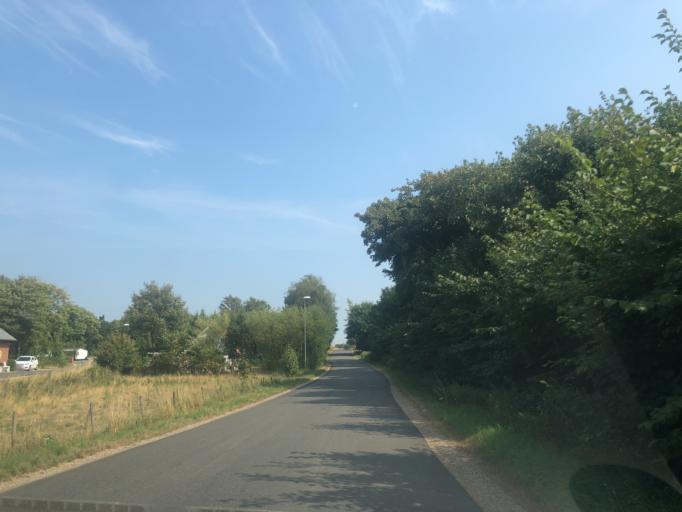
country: DK
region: North Denmark
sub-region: Morso Kommune
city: Nykobing Mors
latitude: 56.8183
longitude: 9.0096
